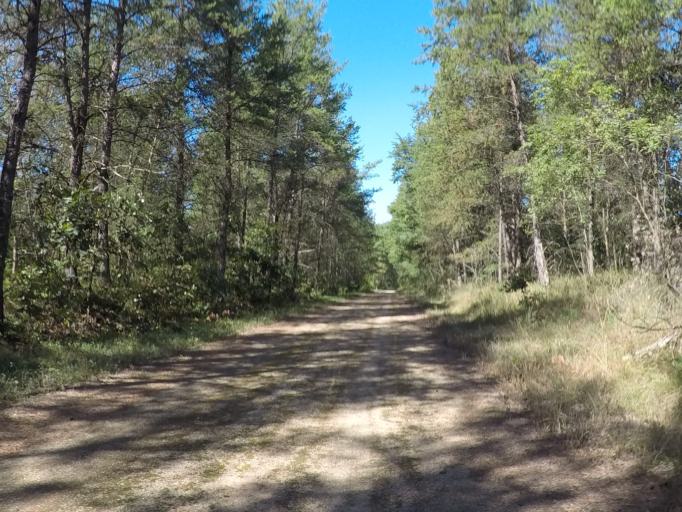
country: US
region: Wisconsin
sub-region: Richland County
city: Richland Center
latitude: 43.2179
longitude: -90.2904
